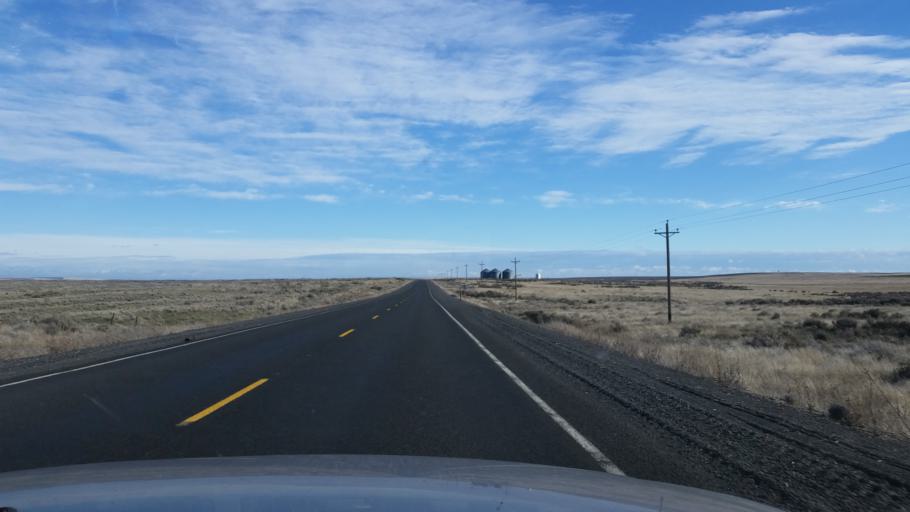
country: US
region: Washington
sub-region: Grant County
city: Warden
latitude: 47.3141
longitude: -118.7875
